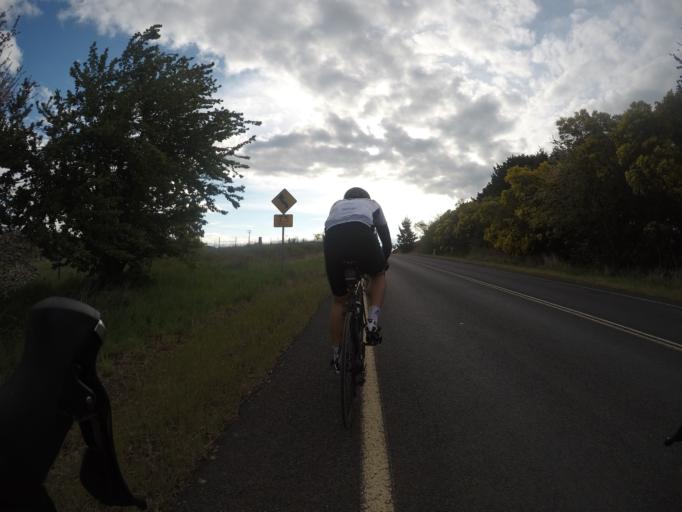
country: AU
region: New South Wales
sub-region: Orange Municipality
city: Orange
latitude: -33.2890
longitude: 149.0301
